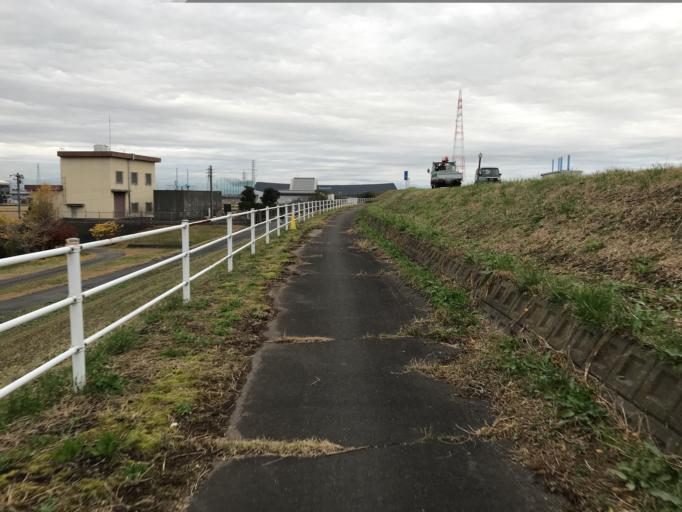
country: JP
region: Gifu
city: Ogaki
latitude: 35.3206
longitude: 136.6665
